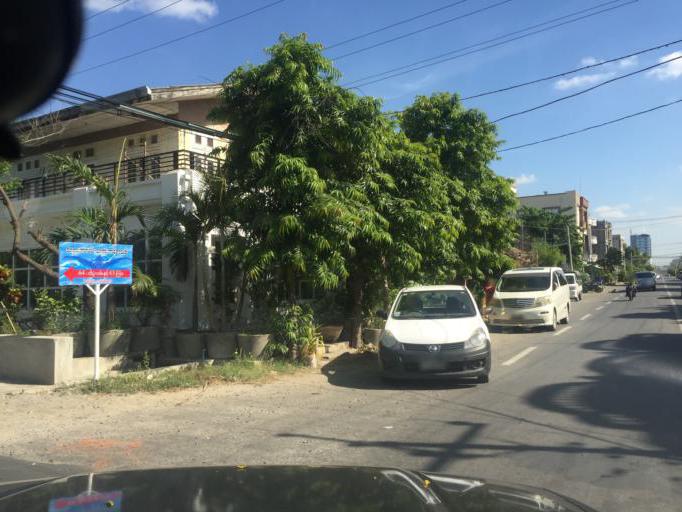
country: MM
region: Mandalay
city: Mandalay
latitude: 21.9535
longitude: 96.1083
